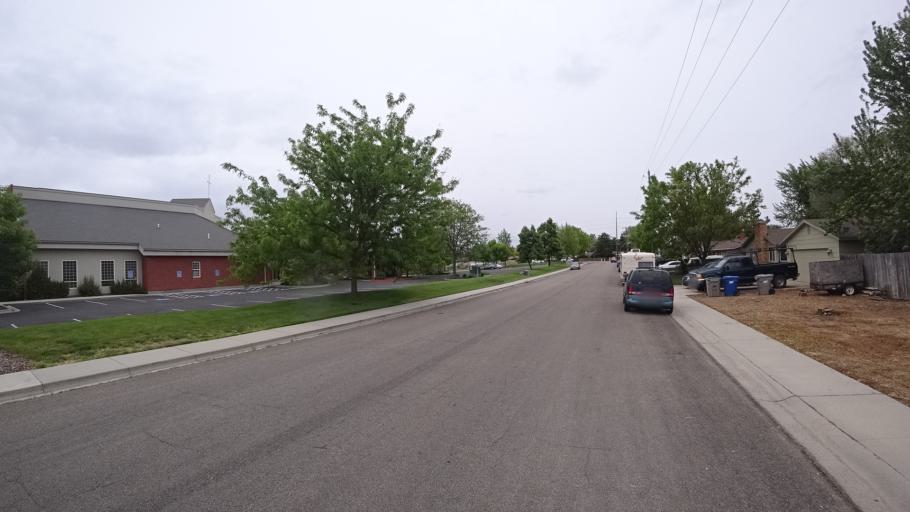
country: US
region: Idaho
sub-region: Ada County
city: Garden City
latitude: 43.6353
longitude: -116.3068
